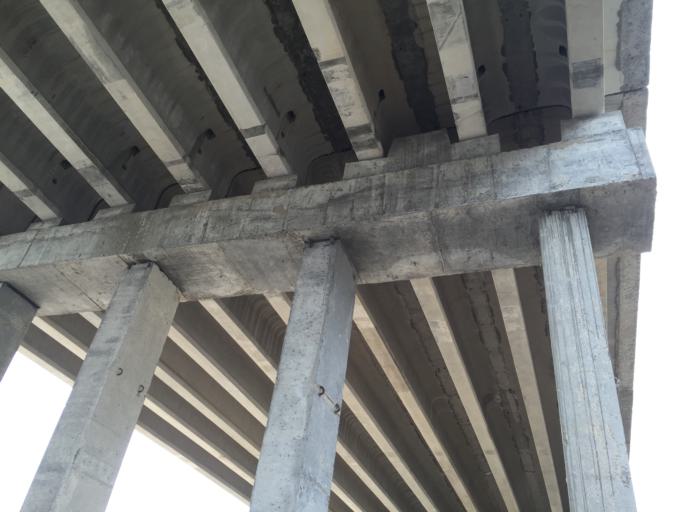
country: KZ
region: Ongtustik Qazaqstan
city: Aksu
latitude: 42.4589
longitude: 69.7604
